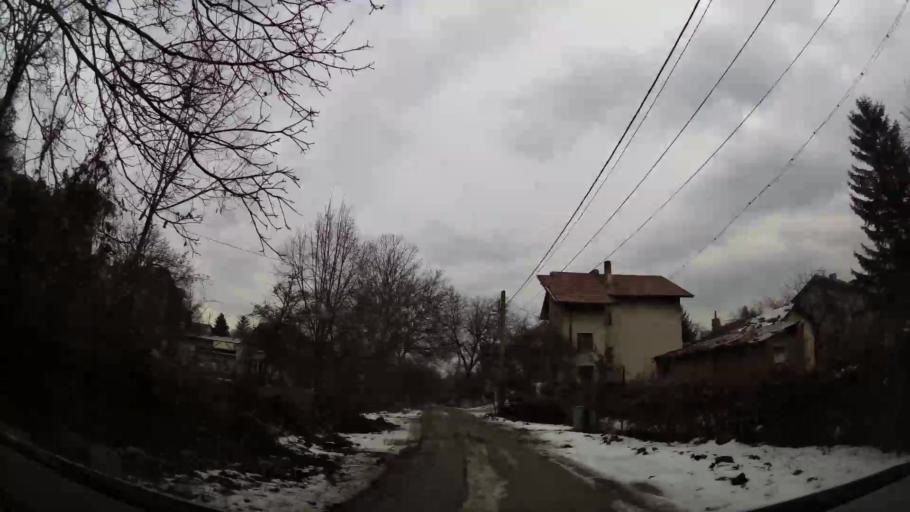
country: BG
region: Sofiya
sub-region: Obshtina Bozhurishte
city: Bozhurishte
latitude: 42.6959
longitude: 23.2187
